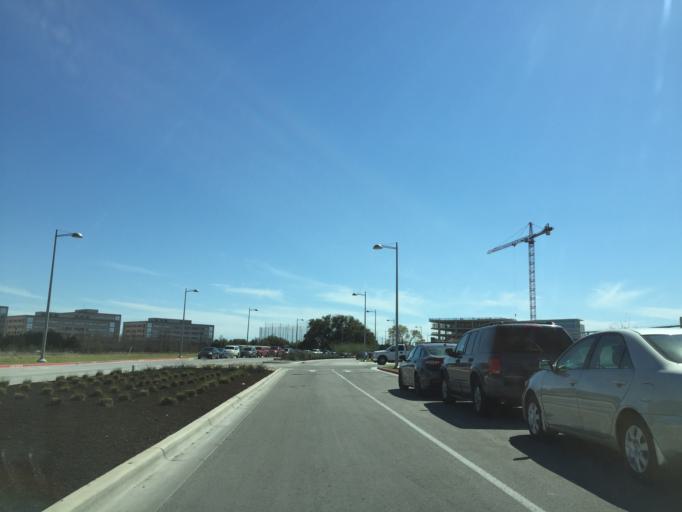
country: US
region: Texas
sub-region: Travis County
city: Wells Branch
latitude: 30.4054
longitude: -97.7190
